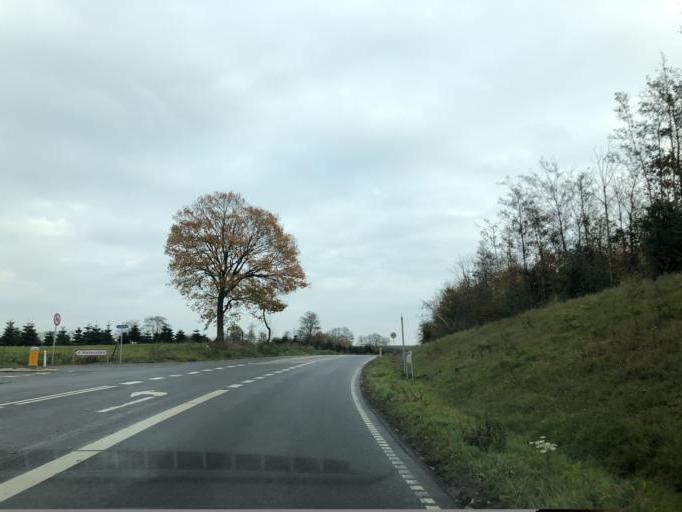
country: DK
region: Central Jutland
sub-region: Hedensted Kommune
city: Hedensted
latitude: 55.7355
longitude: 9.7413
